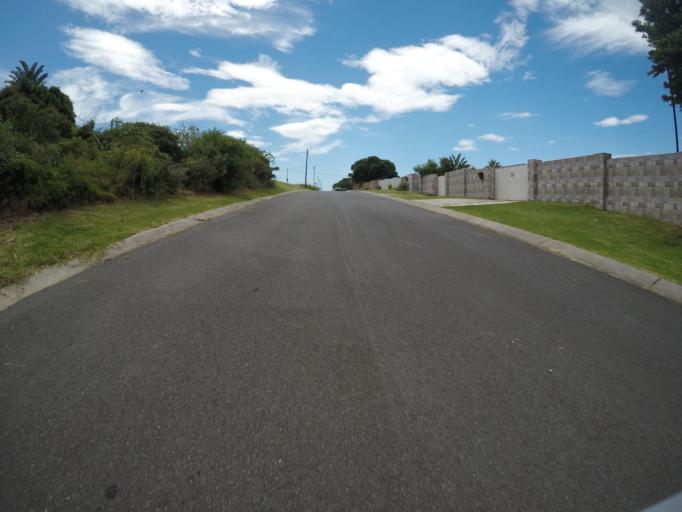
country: ZA
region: Eastern Cape
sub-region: Buffalo City Metropolitan Municipality
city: East London
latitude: -33.0410
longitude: 27.8550
